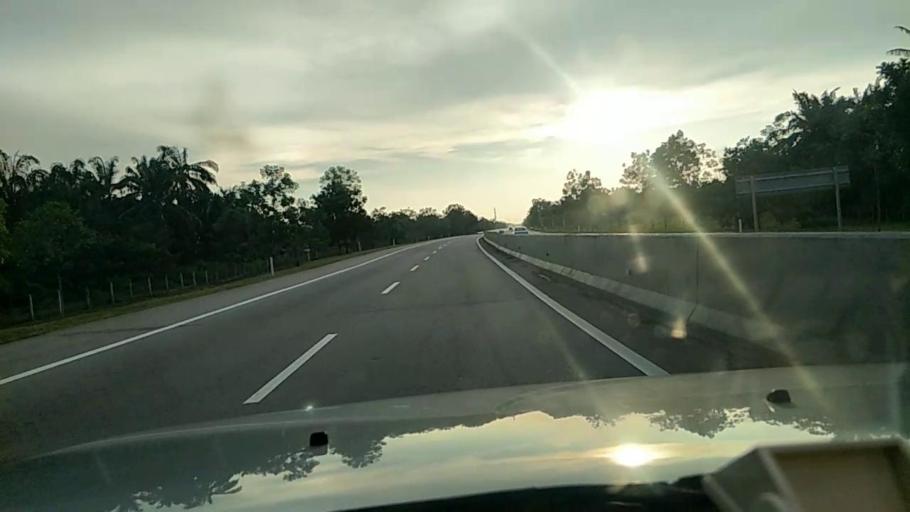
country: MY
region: Selangor
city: Batu Arang
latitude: 3.2877
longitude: 101.4194
